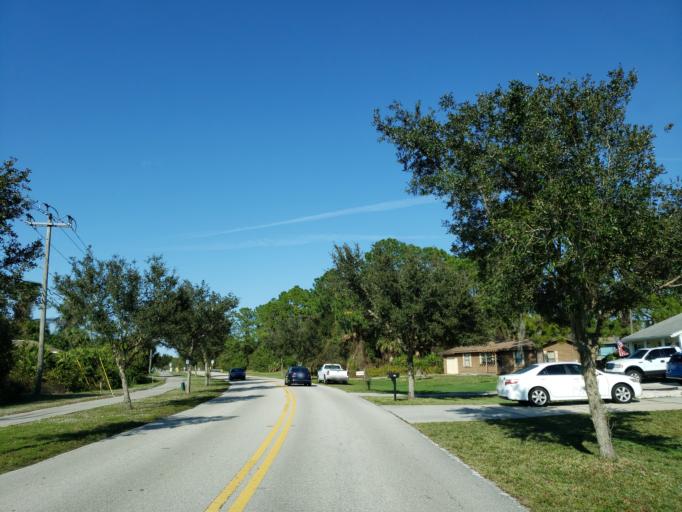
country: US
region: Florida
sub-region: Sarasota County
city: North Port
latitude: 27.0748
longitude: -82.1954
